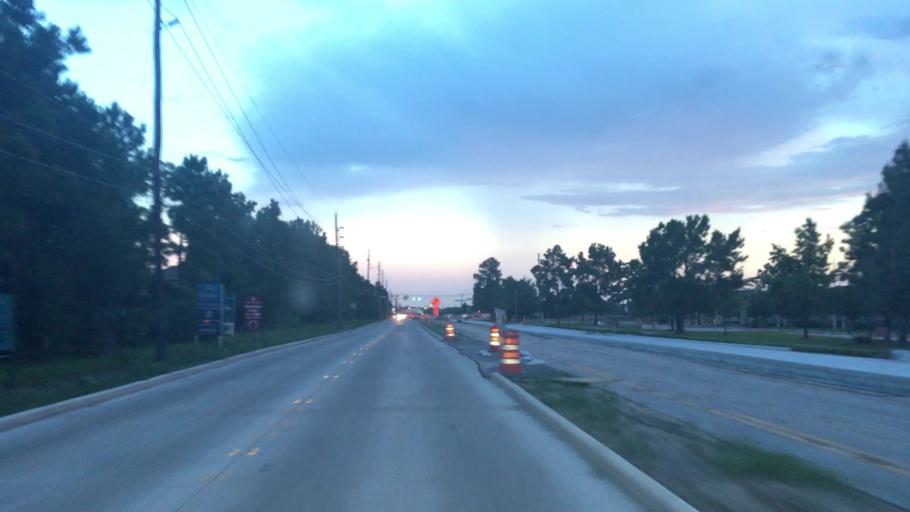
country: US
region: Texas
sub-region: Harris County
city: Humble
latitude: 29.9460
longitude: -95.2496
